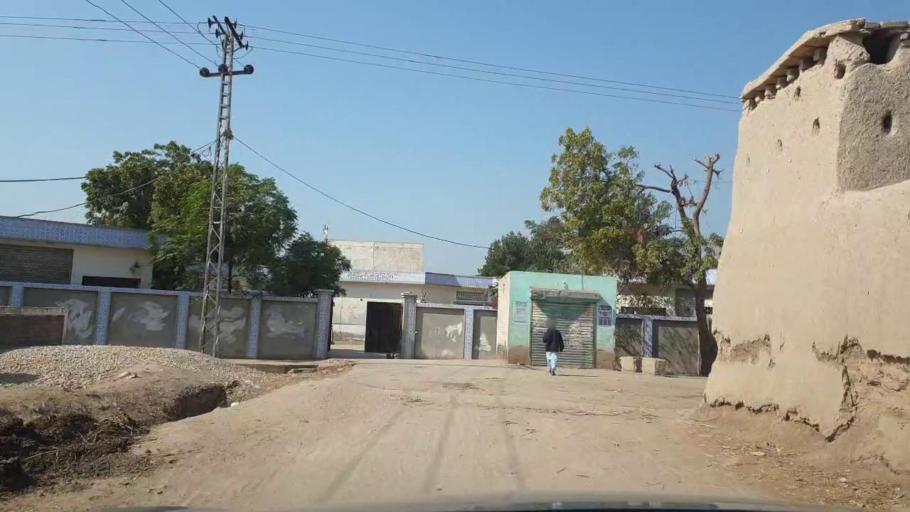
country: PK
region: Sindh
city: Tando Allahyar
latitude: 25.5904
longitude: 68.6945
